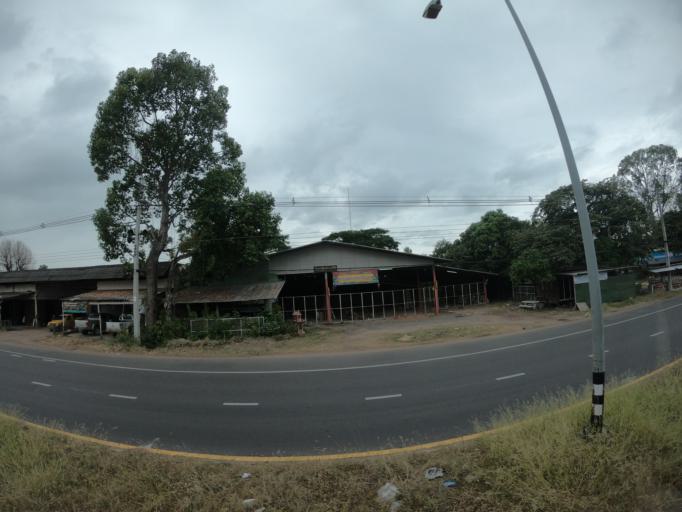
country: TH
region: Roi Et
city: Roi Et
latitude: 16.0438
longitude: 103.6338
